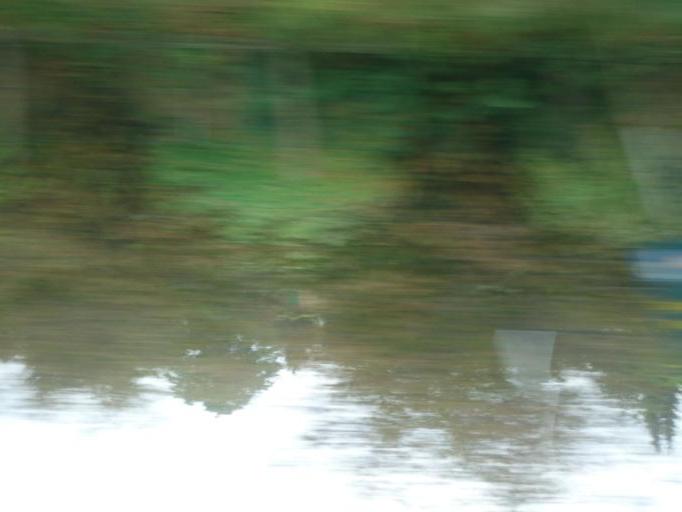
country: DE
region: Saxony-Anhalt
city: Grobers
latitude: 51.4267
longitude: 12.1211
